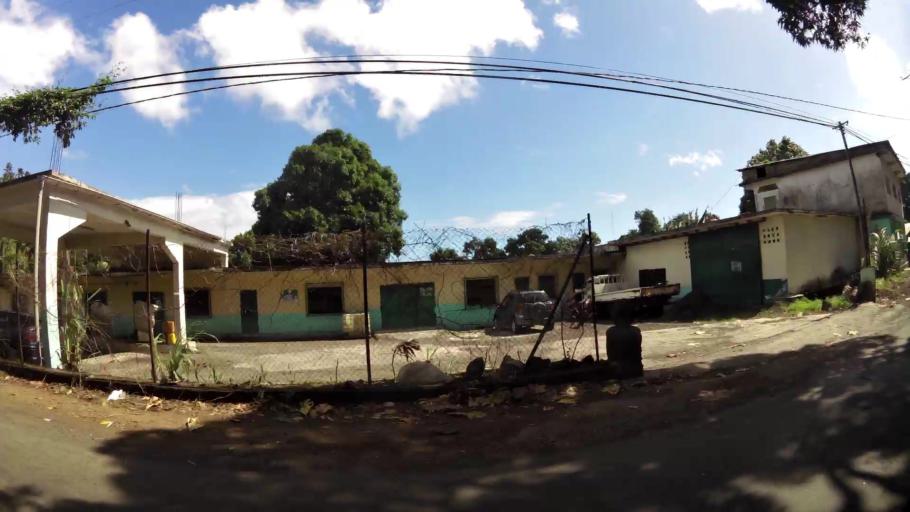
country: KM
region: Grande Comore
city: Mavingouni
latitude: -11.7222
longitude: 43.2506
